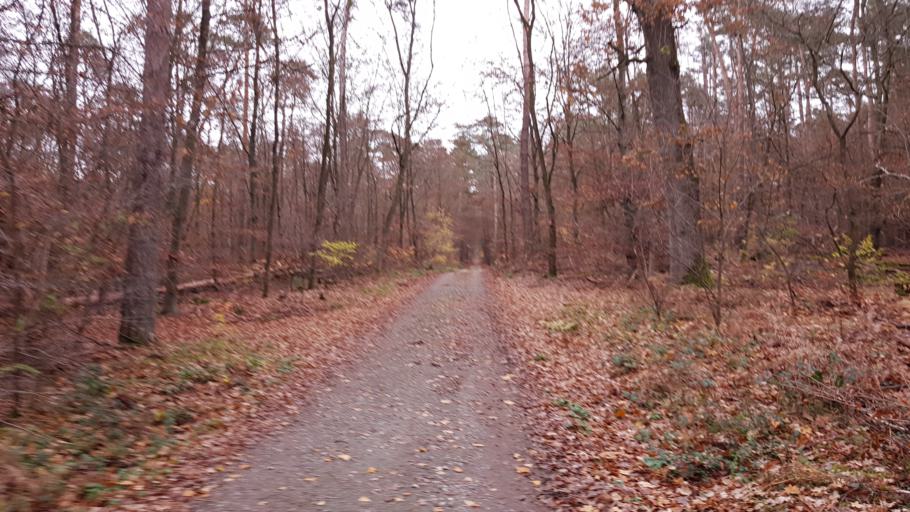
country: DE
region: Hesse
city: Raunheim
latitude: 50.0040
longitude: 8.4716
